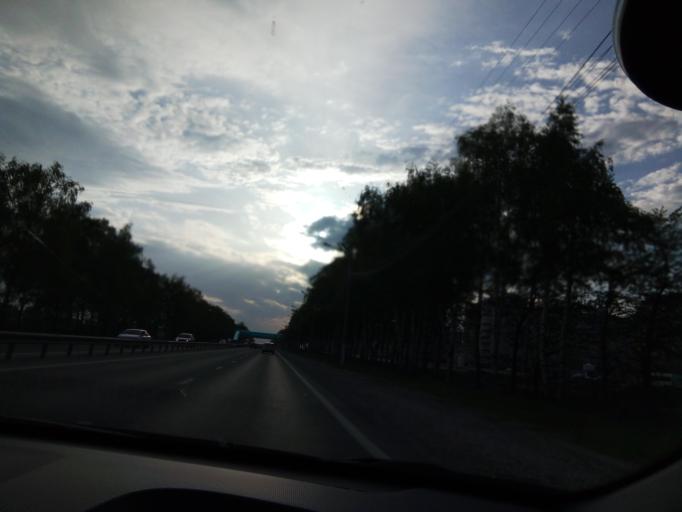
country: RU
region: Chuvashia
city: Novocheboksarsk
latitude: 56.1244
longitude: 47.3876
